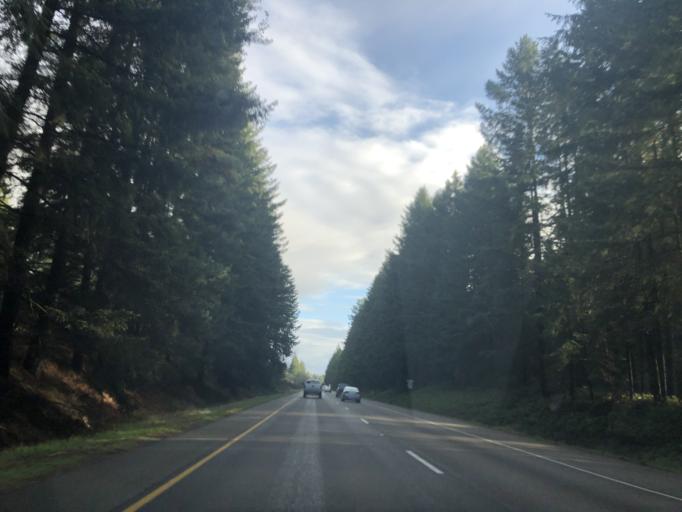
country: US
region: Washington
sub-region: Kitsap County
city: Bethel
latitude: 47.4955
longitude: -122.6405
